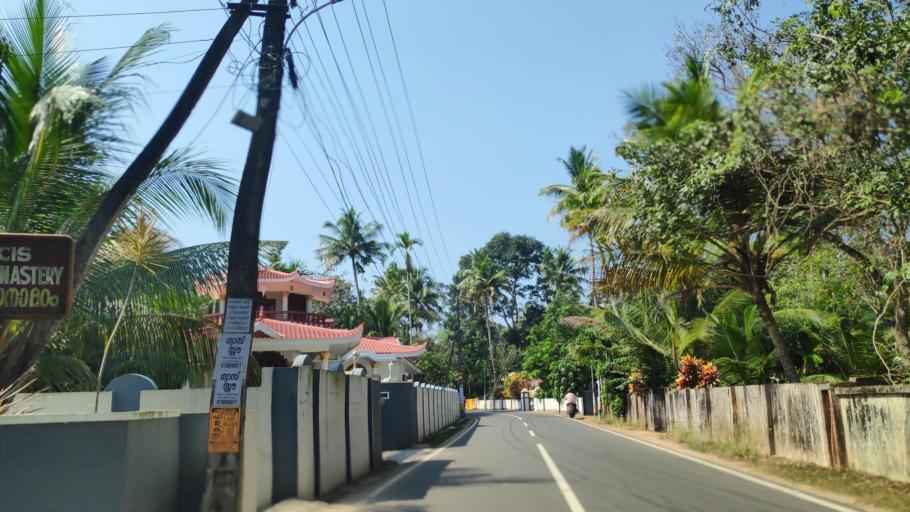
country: IN
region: Kerala
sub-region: Alappuzha
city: Shertallai
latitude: 9.6562
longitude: 76.3365
